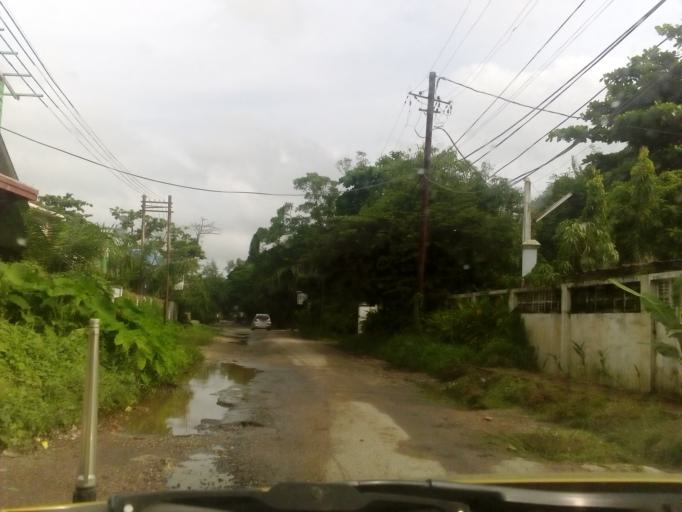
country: MM
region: Yangon
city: Yangon
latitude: 16.8460
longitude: 96.1525
